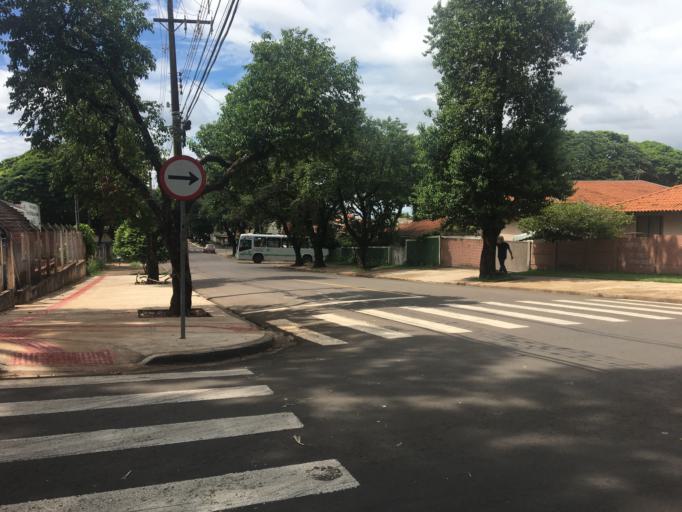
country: BR
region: Parana
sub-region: Maringa
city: Maringa
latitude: -23.4514
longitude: -51.9612
